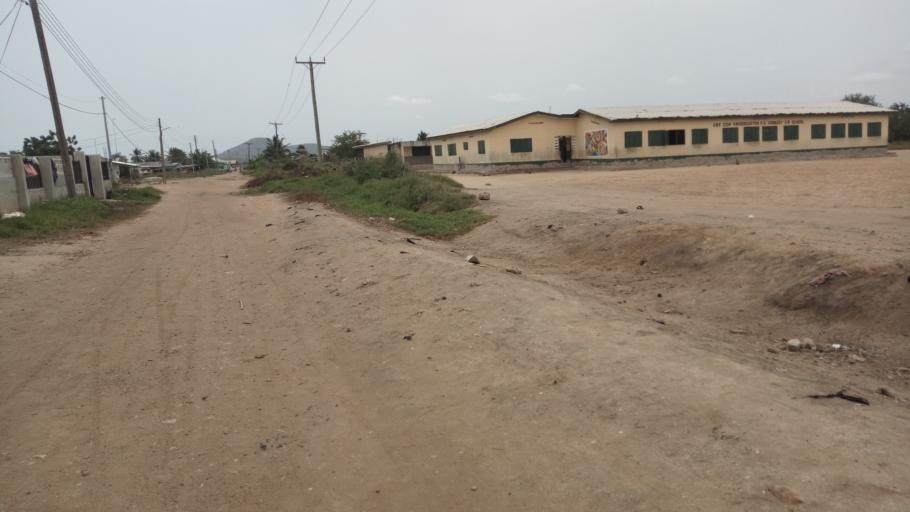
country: GH
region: Central
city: Winneba
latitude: 5.3488
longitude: -0.6311
